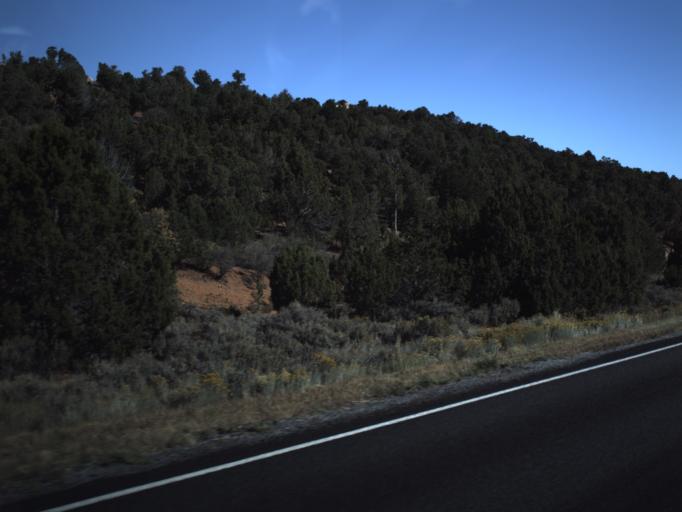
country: US
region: Utah
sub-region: Iron County
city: Cedar City
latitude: 37.6171
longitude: -113.3337
